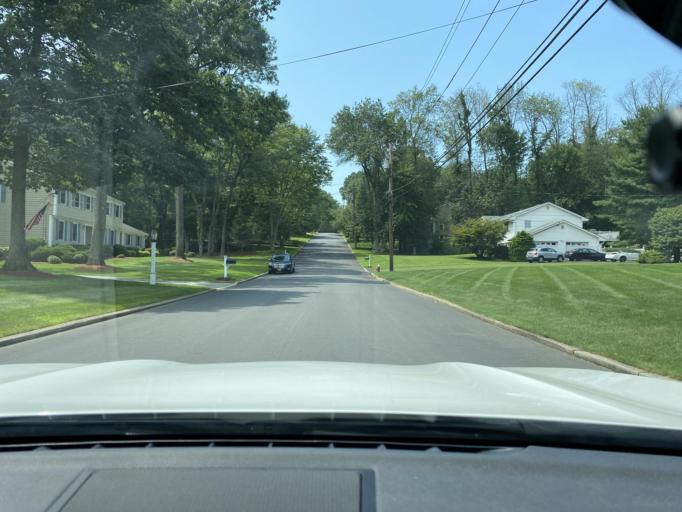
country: US
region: New York
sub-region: Rockland County
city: Airmont
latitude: 41.0813
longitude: -74.1086
